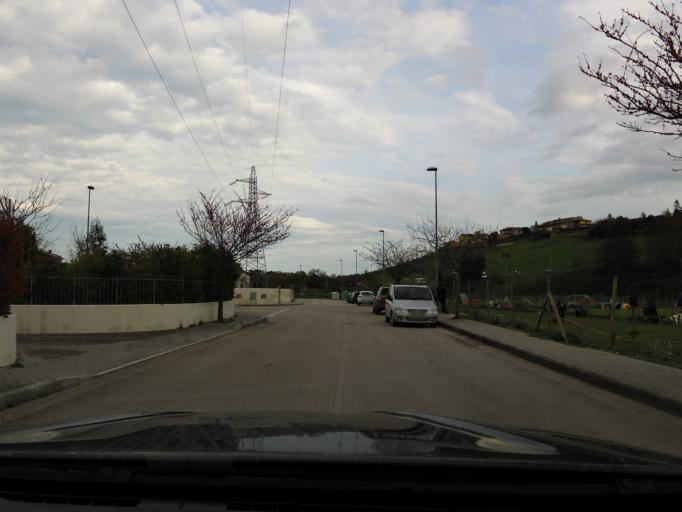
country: IT
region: The Marches
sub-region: Provincia di Ancona
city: Loreto Stazione
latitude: 43.4452
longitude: 13.6229
